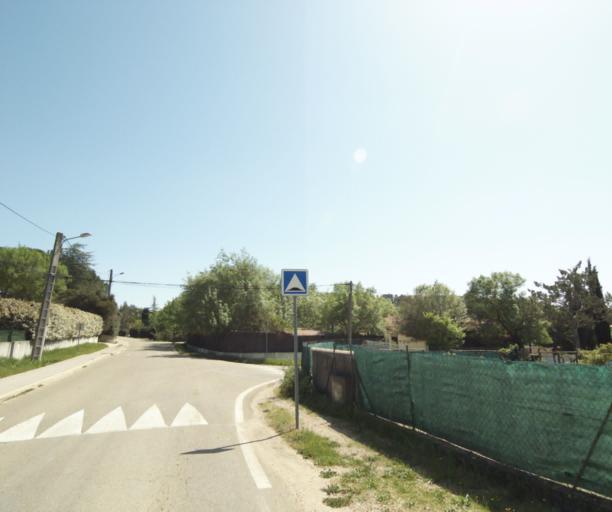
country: FR
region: Languedoc-Roussillon
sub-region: Departement de l'Herault
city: Prades-le-Lez
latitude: 43.6926
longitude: 3.8746
